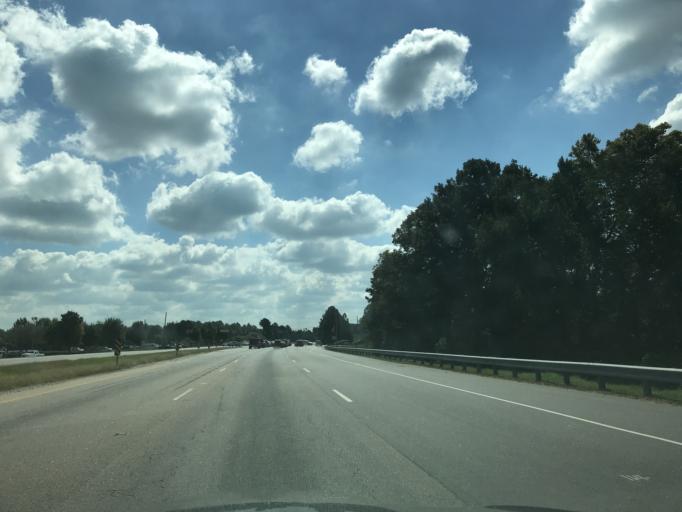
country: US
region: North Carolina
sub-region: Wake County
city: Wake Forest
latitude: 35.9478
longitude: -78.5393
